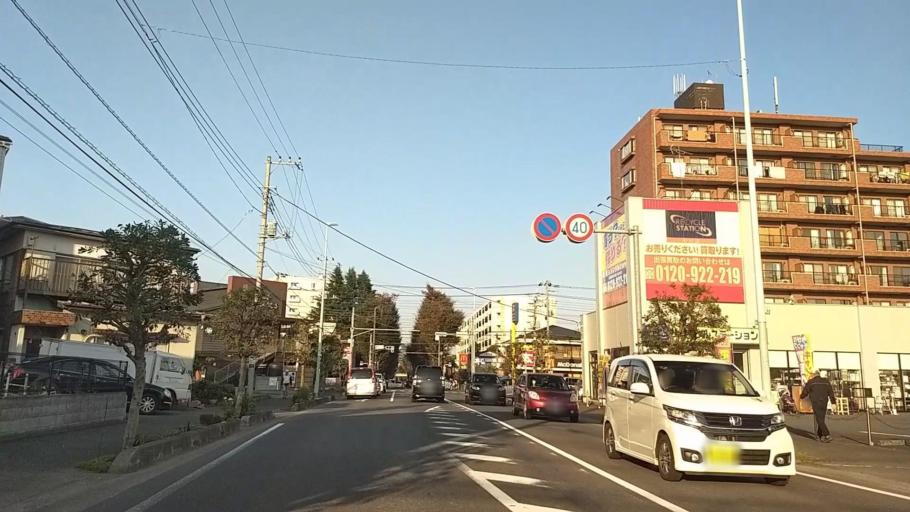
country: JP
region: Saitama
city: Tokorozawa
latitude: 35.7998
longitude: 139.4476
